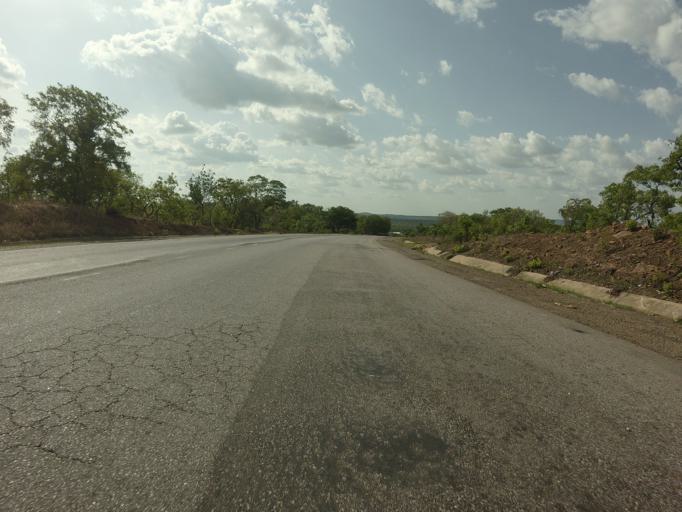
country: GH
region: Upper East
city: Bolgatanga
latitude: 10.5528
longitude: -0.8300
